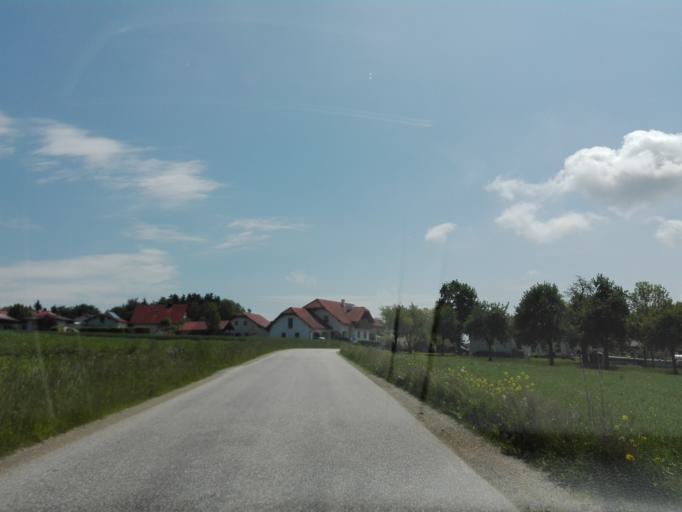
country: AT
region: Upper Austria
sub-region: Politischer Bezirk Rohrbach
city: Atzesberg
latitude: 48.4171
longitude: 13.9137
